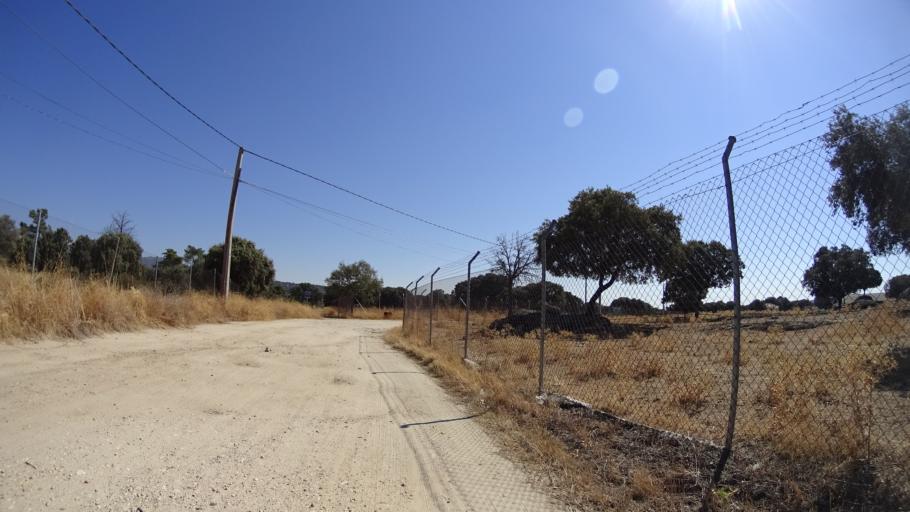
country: ES
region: Madrid
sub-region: Provincia de Madrid
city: Collado-Villalba
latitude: 40.6152
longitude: -4.0003
